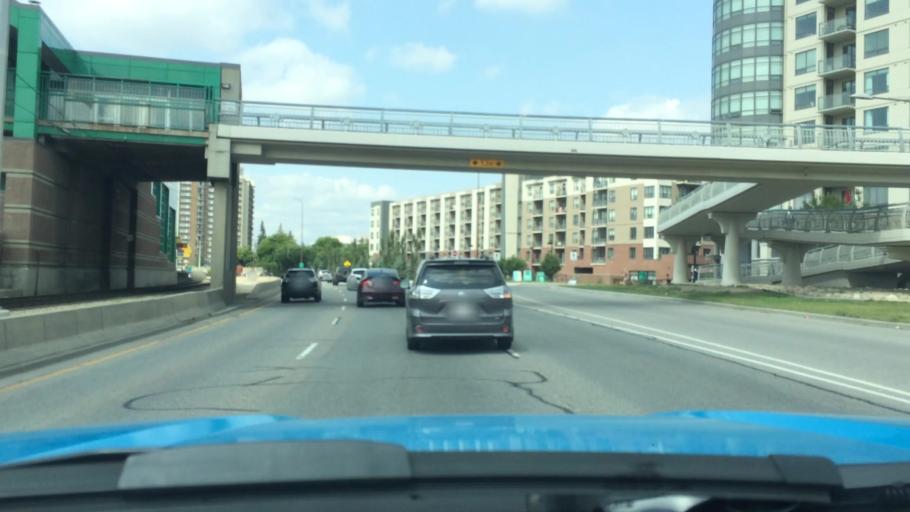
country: CA
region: Alberta
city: Calgary
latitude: 51.0490
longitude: -114.0393
